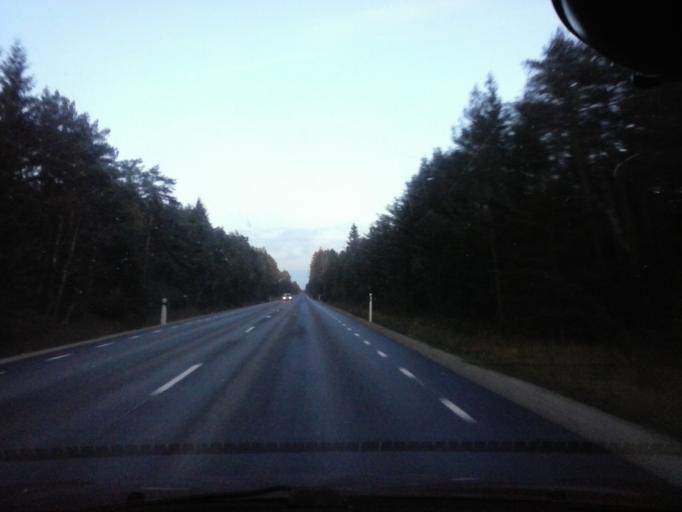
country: EE
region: Raplamaa
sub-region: Maerjamaa vald
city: Marjamaa
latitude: 58.9296
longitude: 24.5119
